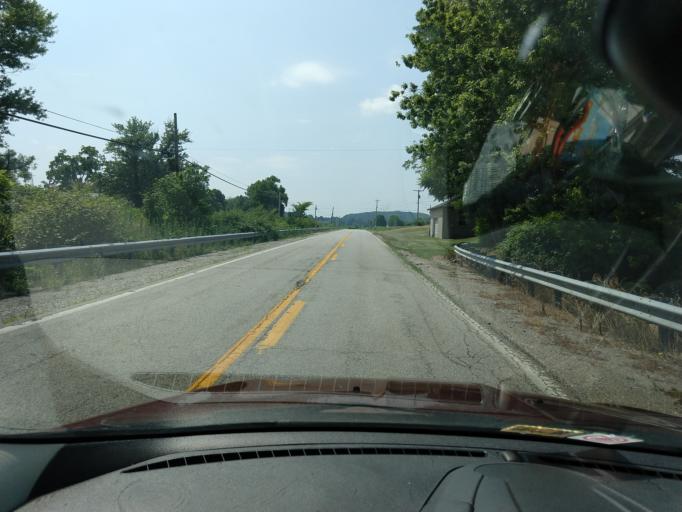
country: US
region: West Virginia
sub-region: Mason County
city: New Haven
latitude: 38.8934
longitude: -81.9332
